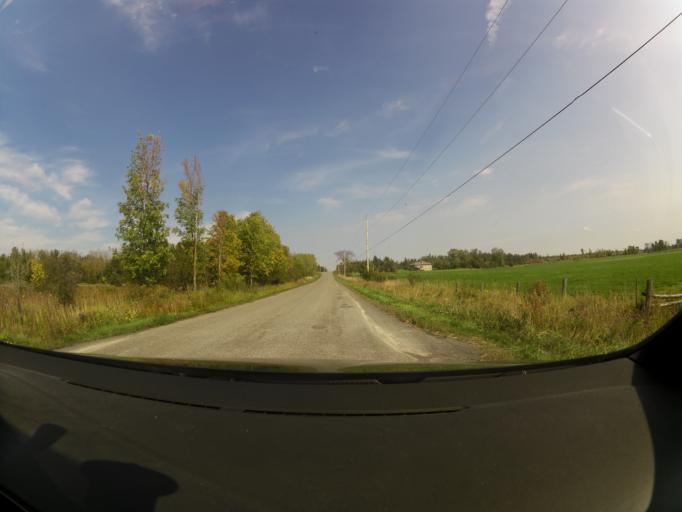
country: CA
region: Ontario
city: Carleton Place
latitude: 45.2926
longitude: -76.2280
